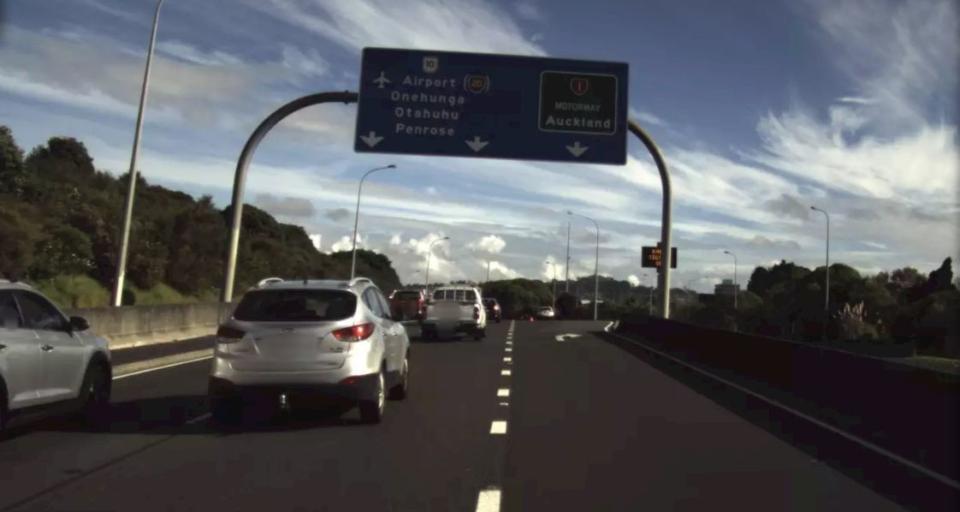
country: NZ
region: Auckland
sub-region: Auckland
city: Tamaki
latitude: -36.9163
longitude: 174.8295
